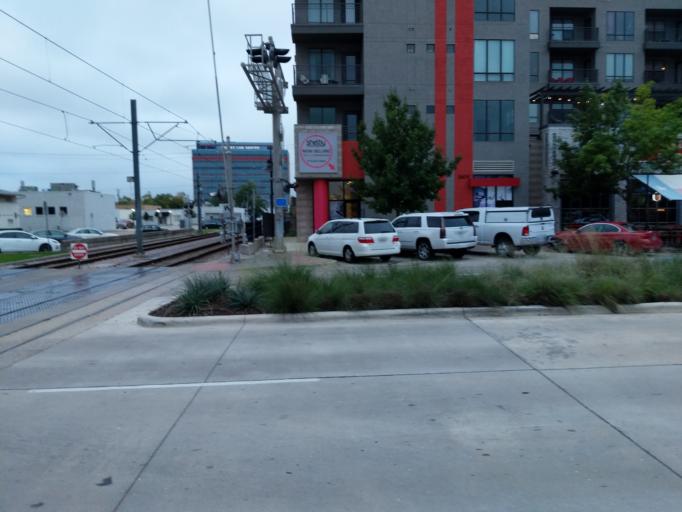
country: US
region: Texas
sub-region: Dallas County
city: Highland Park
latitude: 32.8419
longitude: -96.7725
